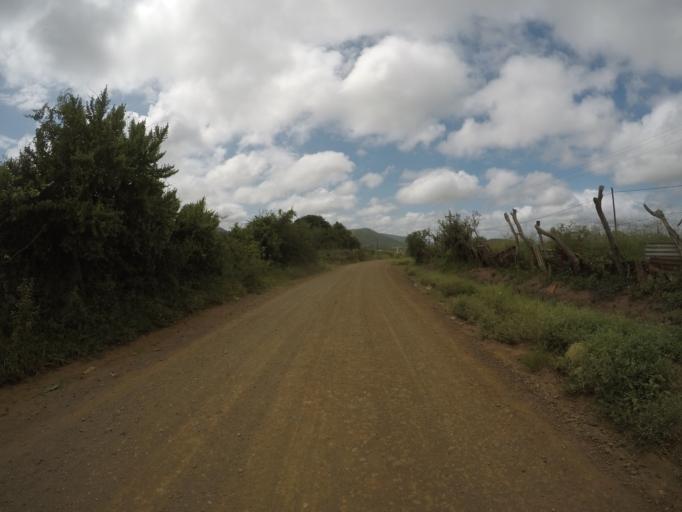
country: ZA
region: KwaZulu-Natal
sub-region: uThungulu District Municipality
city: Empangeni
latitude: -28.5775
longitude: 31.8462
